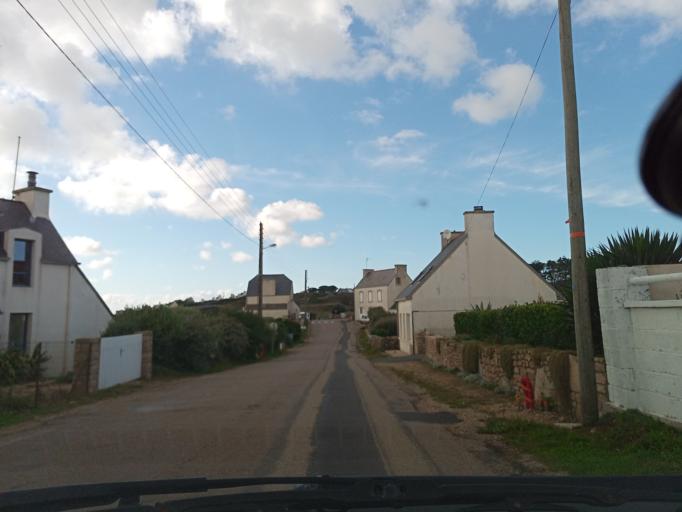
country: FR
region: Brittany
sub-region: Departement du Finistere
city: Plouhinec
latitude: 47.9846
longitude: -4.4604
